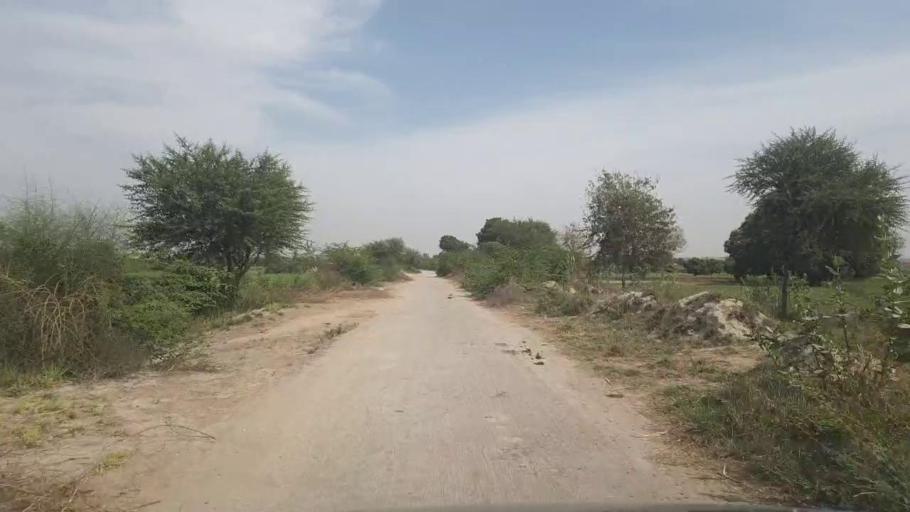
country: PK
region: Sindh
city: Kunri
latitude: 25.2021
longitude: 69.6837
